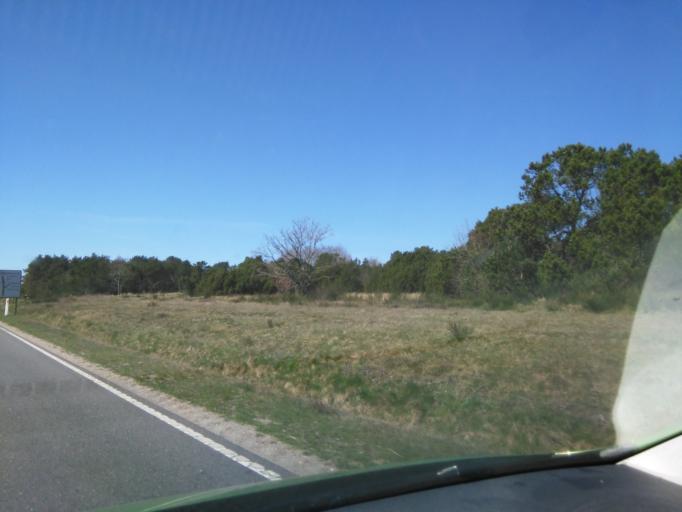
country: DK
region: South Denmark
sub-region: Varde Kommune
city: Oksbol
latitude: 55.6152
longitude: 8.2484
